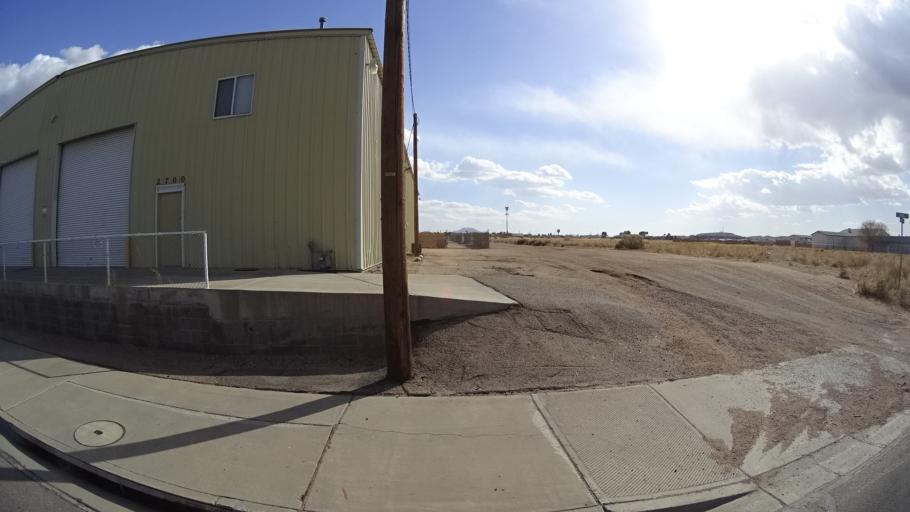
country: US
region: Arizona
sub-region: Mohave County
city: New Kingman-Butler
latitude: 35.2248
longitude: -114.0158
